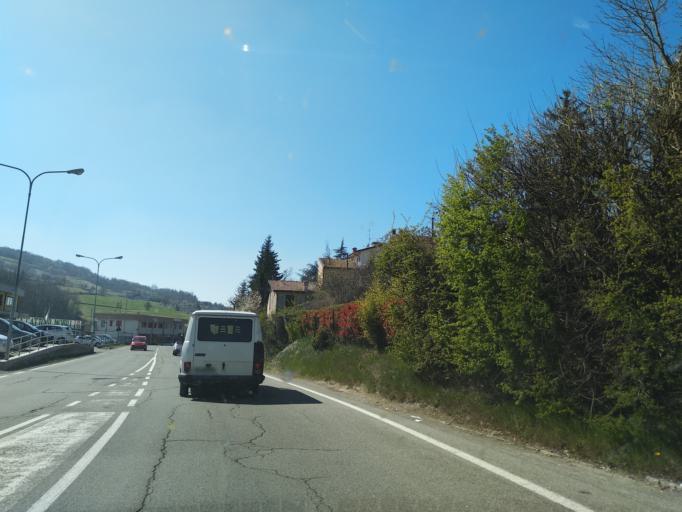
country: IT
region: Emilia-Romagna
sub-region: Provincia di Reggio Emilia
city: Castelnovo ne'Monti
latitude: 44.4369
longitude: 10.4309
